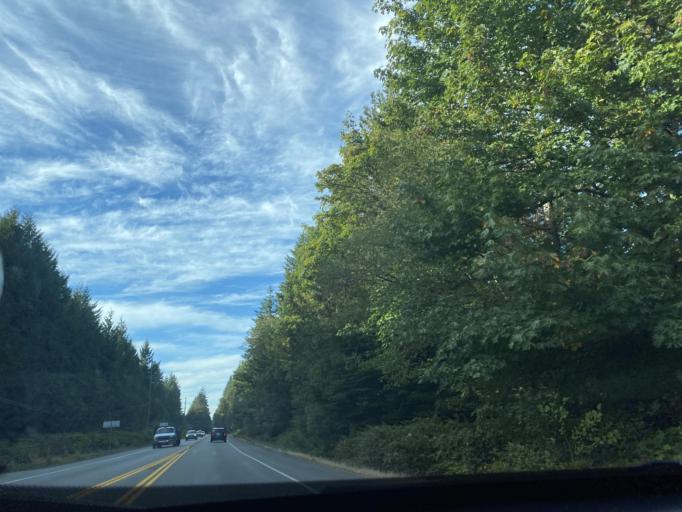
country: US
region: Washington
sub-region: Kitsap County
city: Suquamish
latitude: 47.6802
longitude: -122.5400
